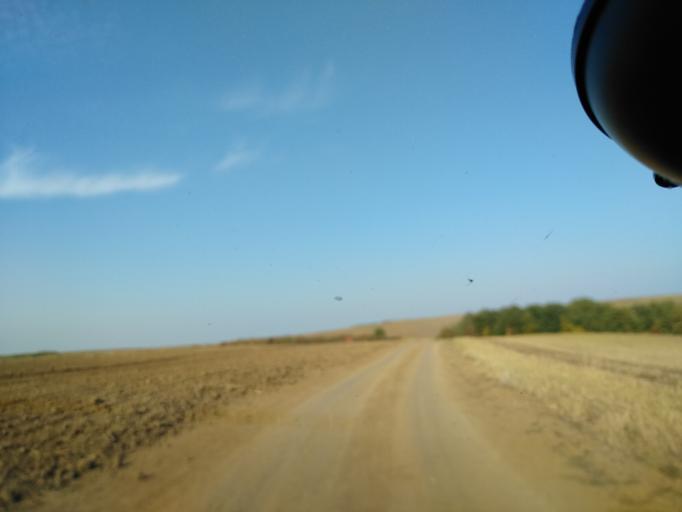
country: RO
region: Timis
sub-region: Oras Recas
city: Recas
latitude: 45.8821
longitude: 21.5421
